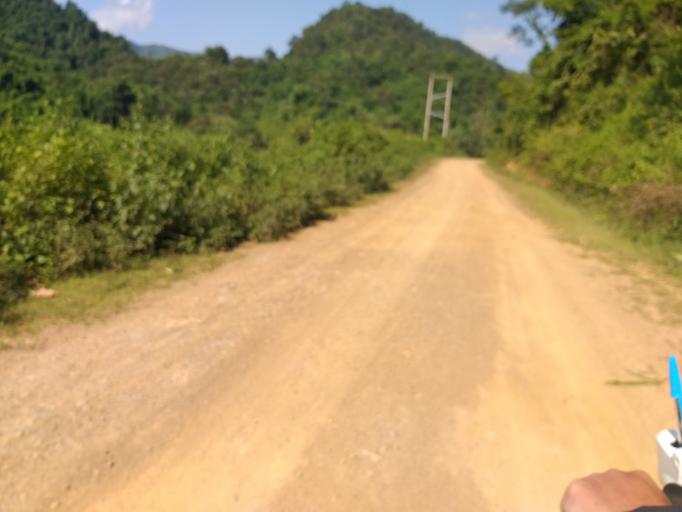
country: LA
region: Phongsali
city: Khoa
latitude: 21.1948
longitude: 102.6433
